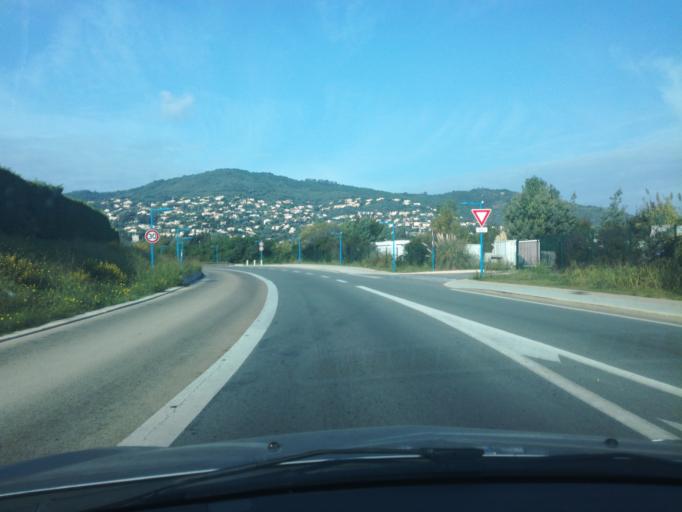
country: FR
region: Provence-Alpes-Cote d'Azur
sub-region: Departement des Alpes-Maritimes
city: Mandelieu-la-Napoule
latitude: 43.5571
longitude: 6.9513
